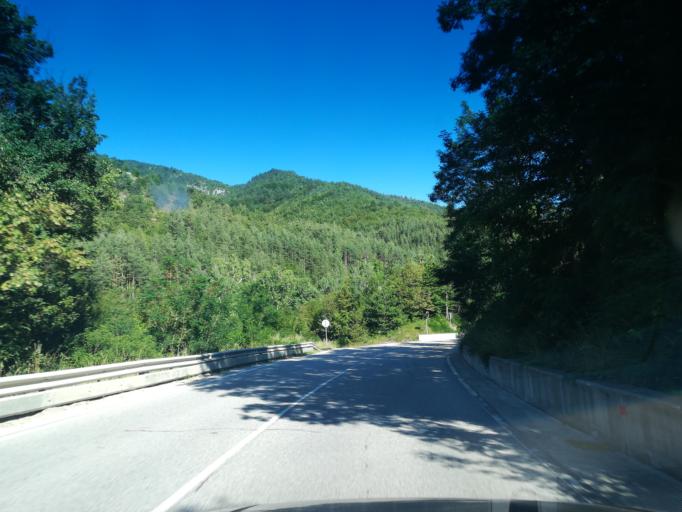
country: BG
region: Smolyan
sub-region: Obshtina Chepelare
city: Chepelare
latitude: 41.8360
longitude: 24.6825
